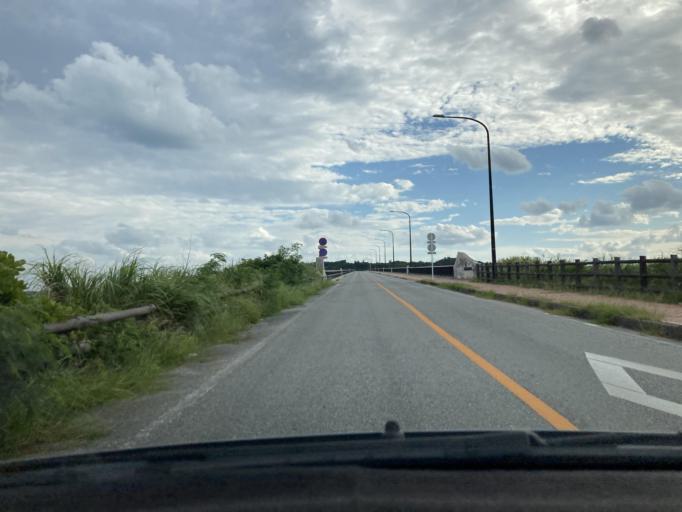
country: JP
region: Okinawa
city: Katsuren-haebaru
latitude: 26.3374
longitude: 127.9553
